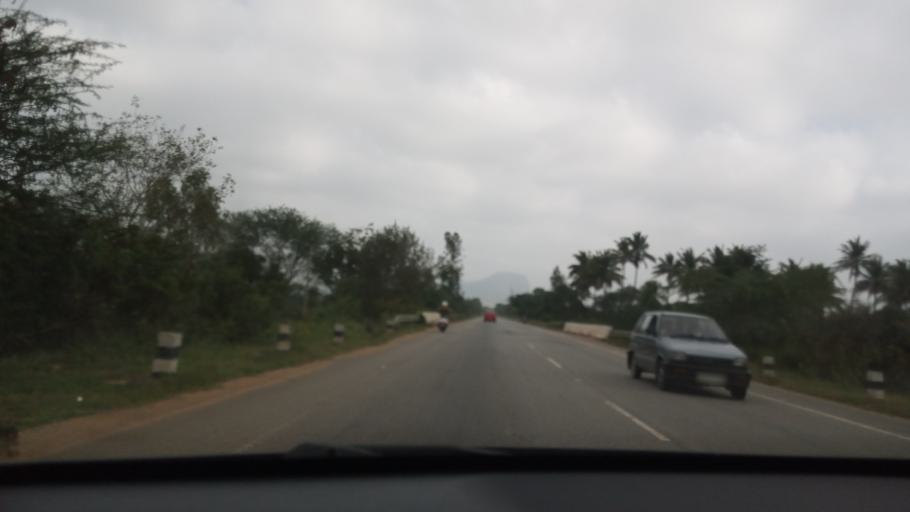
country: IN
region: Karnataka
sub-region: Chikkaballapur
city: Chintamani
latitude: 13.3070
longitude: 77.9748
